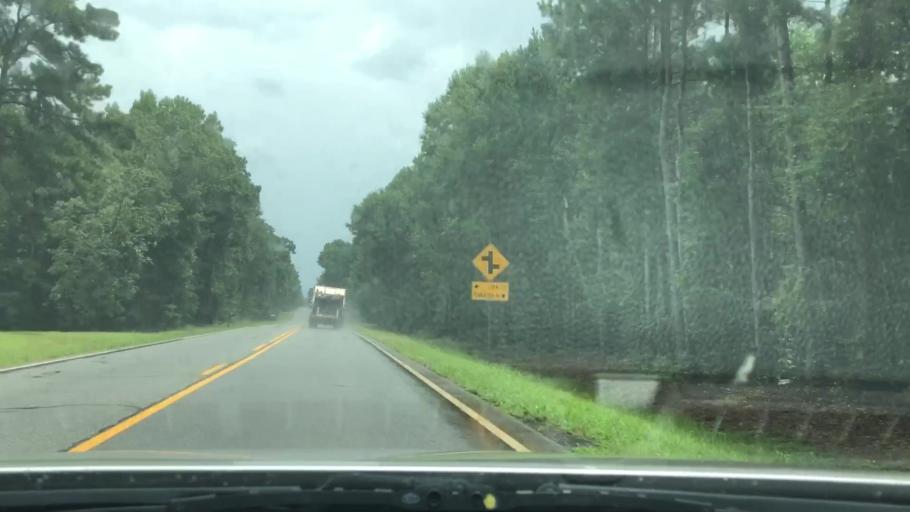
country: US
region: Georgia
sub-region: Pike County
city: Zebulon
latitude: 33.0772
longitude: -84.2522
